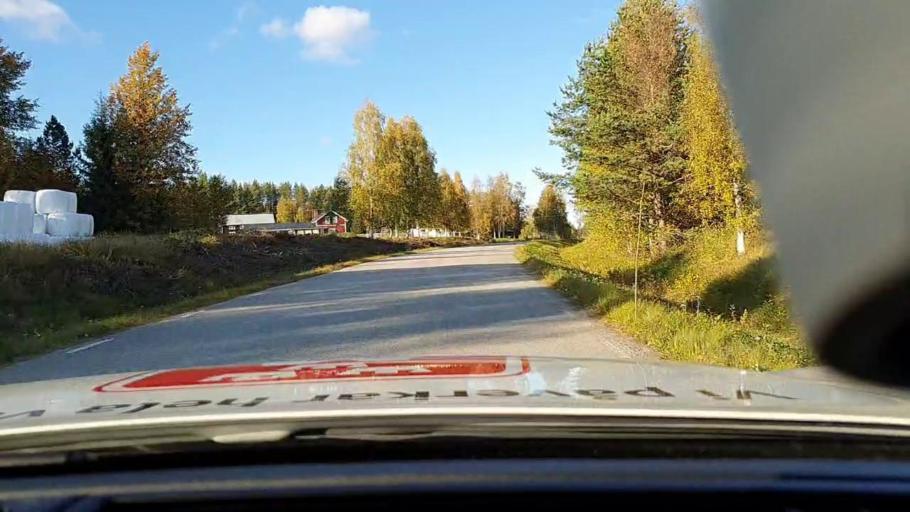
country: SE
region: Norrbotten
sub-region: Pitea Kommun
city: Norrfjarden
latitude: 65.5271
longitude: 21.4873
